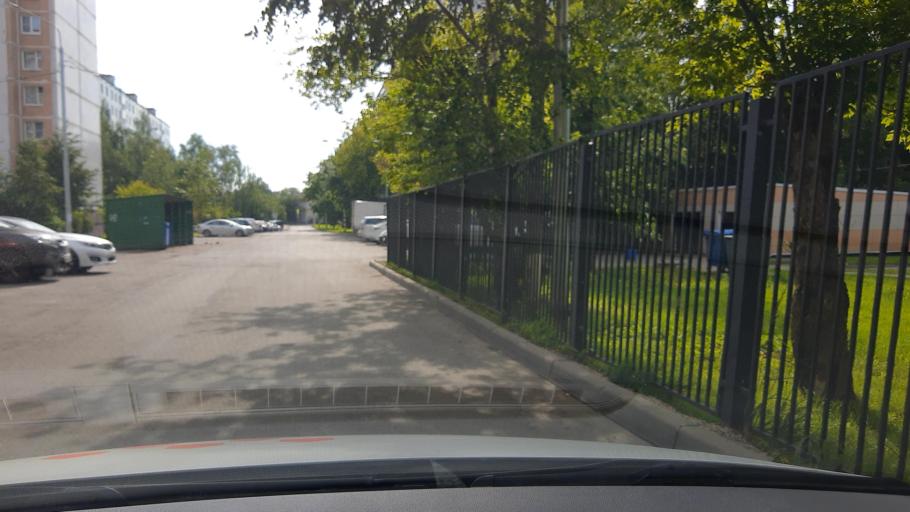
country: RU
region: Moskovskaya
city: Kokoshkino
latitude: 55.6030
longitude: 37.1668
